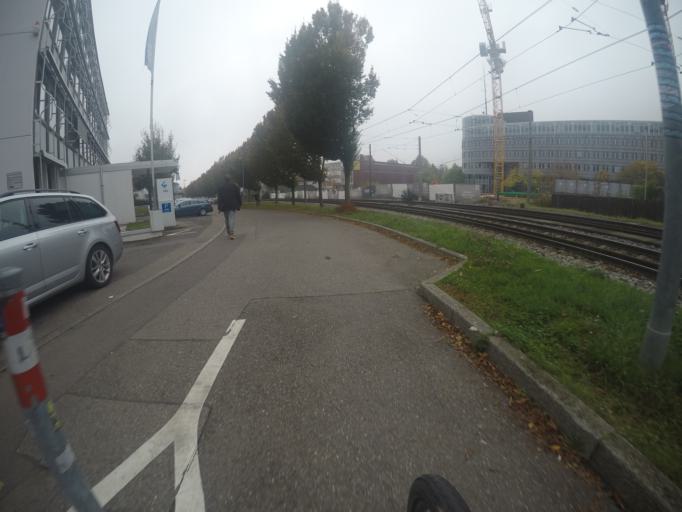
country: DE
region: Baden-Wuerttemberg
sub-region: Regierungsbezirk Stuttgart
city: Leinfelden-Echterdingen
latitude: 48.7285
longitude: 9.1191
